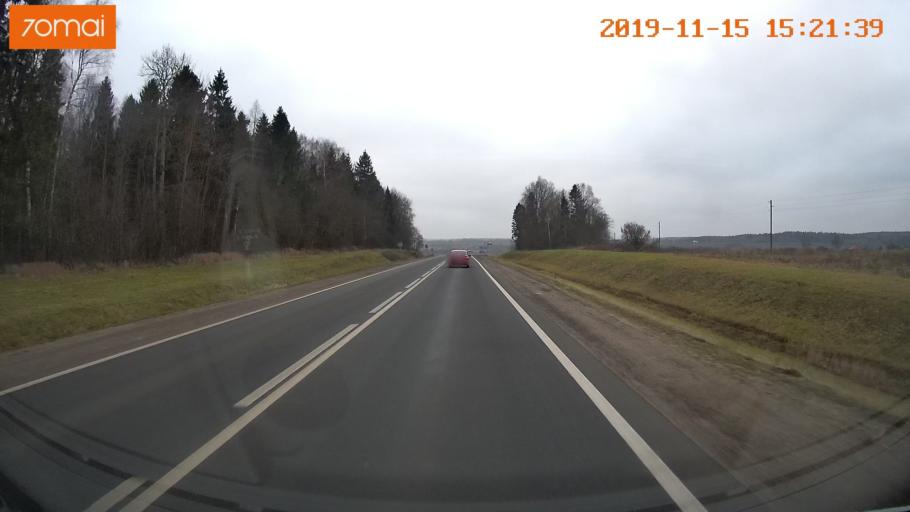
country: RU
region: Jaroslavl
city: Danilov
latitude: 58.2104
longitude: 40.1424
